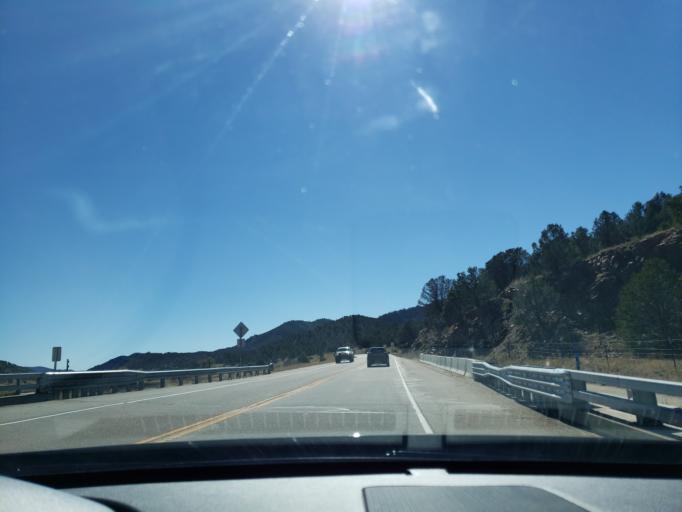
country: US
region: Colorado
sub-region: Fremont County
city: Canon City
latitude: 38.6174
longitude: -105.4451
